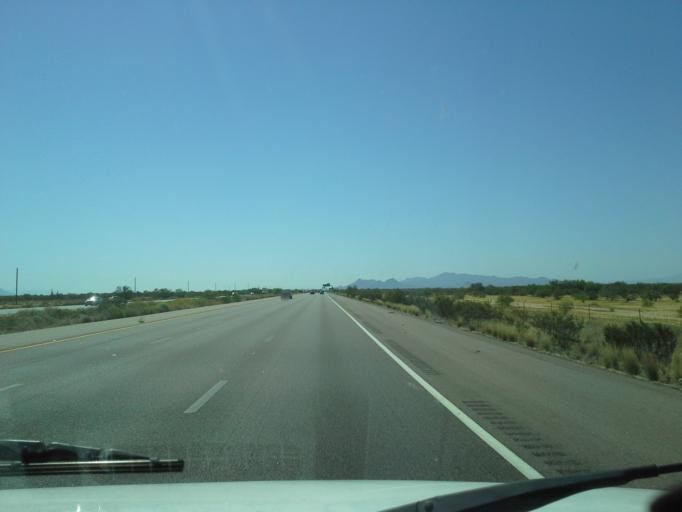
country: US
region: Arizona
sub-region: Pima County
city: Avra Valley
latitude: 32.5273
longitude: -111.2848
